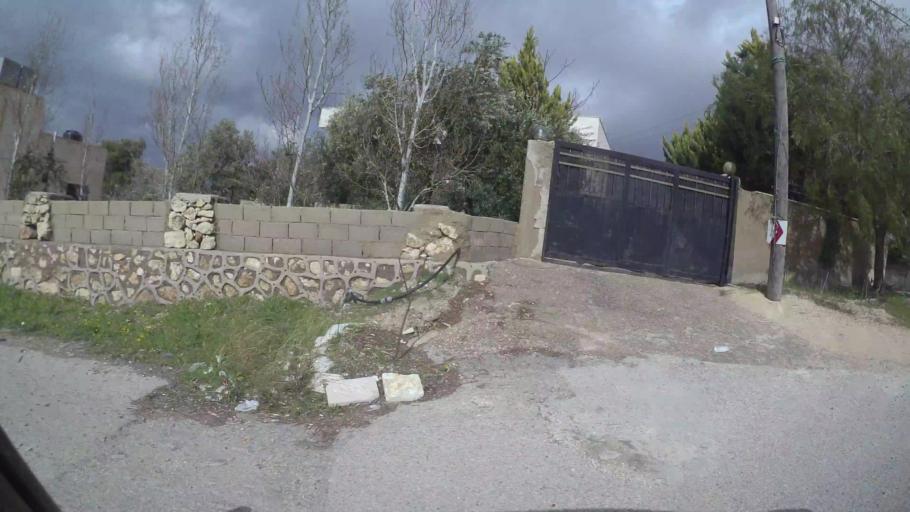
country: JO
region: Amman
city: Al Jubayhah
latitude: 32.0741
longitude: 35.8692
